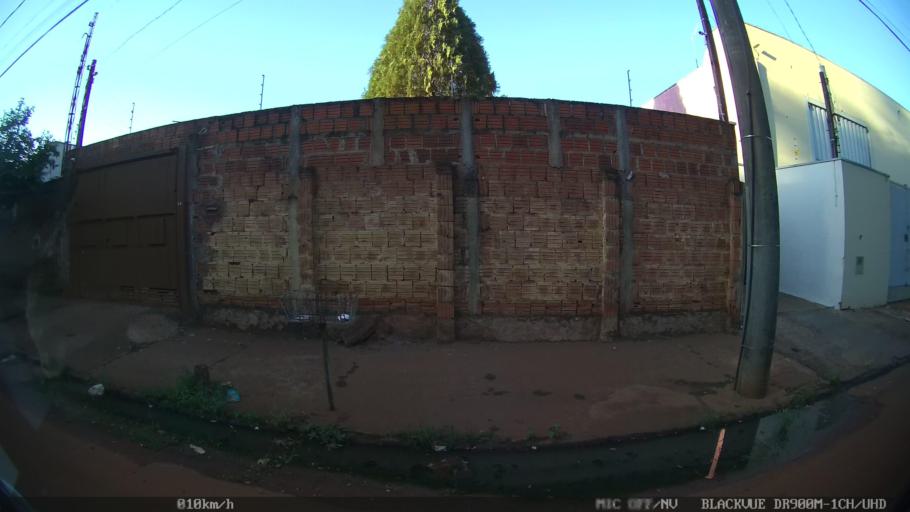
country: BR
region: Sao Paulo
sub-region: Sao Jose Do Rio Preto
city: Sao Jose do Rio Preto
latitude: -20.7745
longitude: -49.3526
